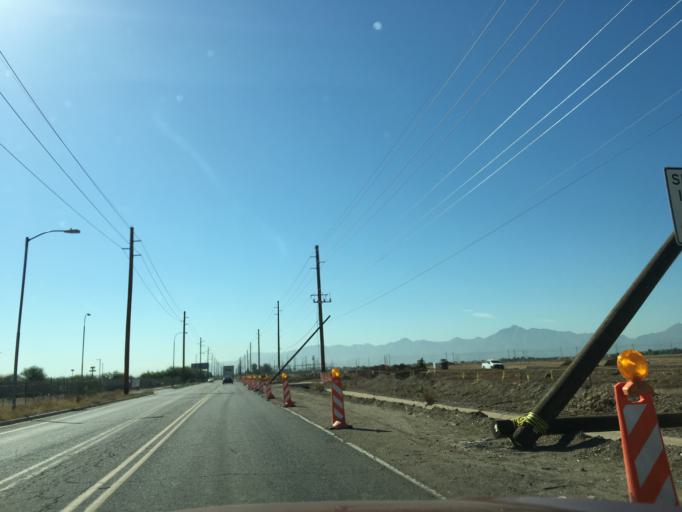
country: US
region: Arizona
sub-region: Maricopa County
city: Laveen
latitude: 33.4297
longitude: -112.1865
